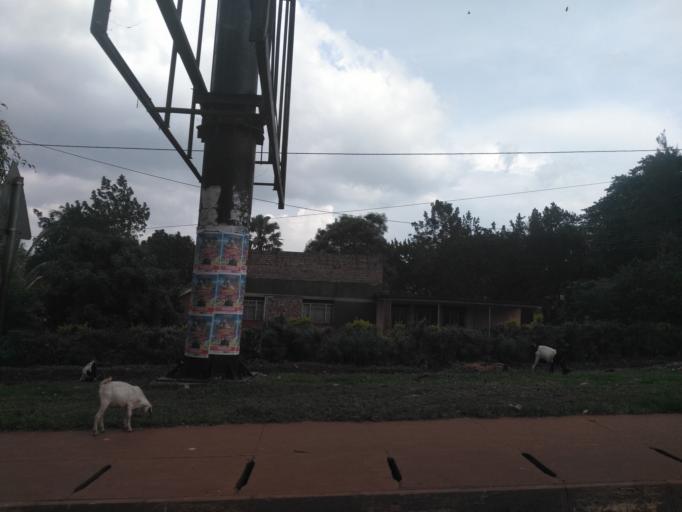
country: UG
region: Eastern Region
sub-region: Jinja District
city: Jinja
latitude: 0.4412
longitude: 33.1998
